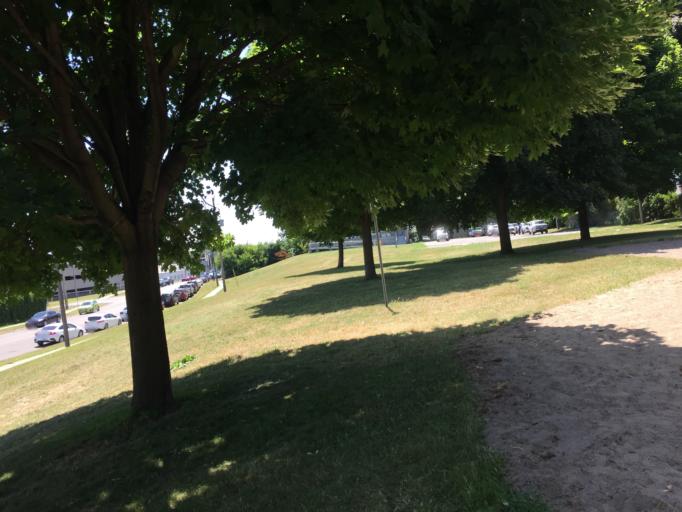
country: CA
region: Ontario
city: Oshawa
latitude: 43.8987
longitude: -78.8720
